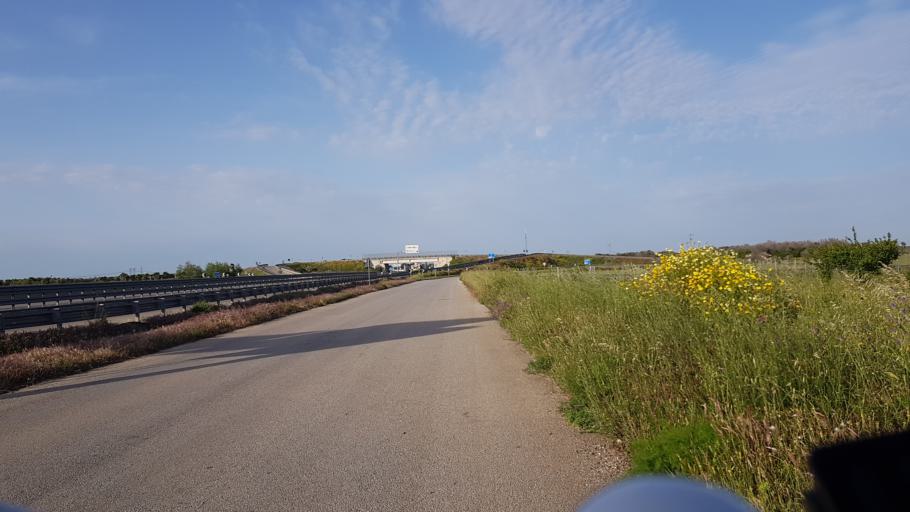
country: IT
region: Apulia
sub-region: Provincia di Brindisi
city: Mesagne
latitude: 40.5892
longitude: 17.8571
